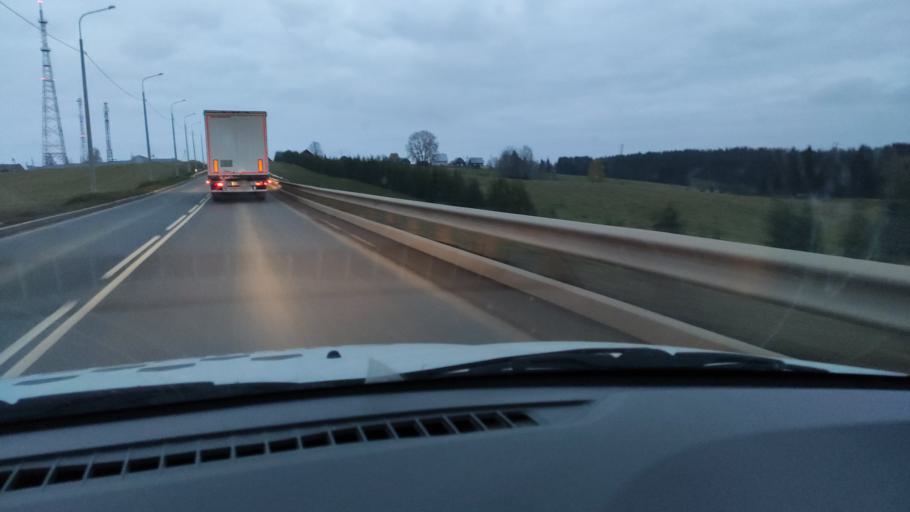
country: RU
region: Kirov
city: Kostino
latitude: 58.8505
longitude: 53.2788
